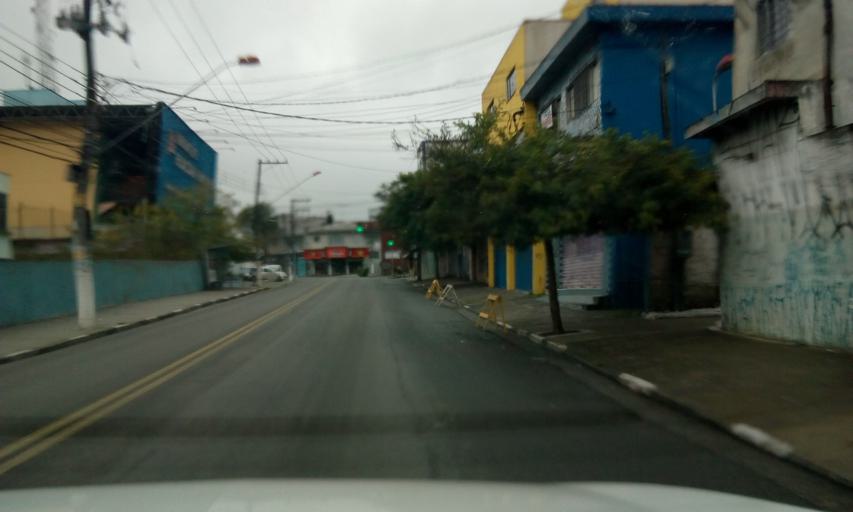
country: BR
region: Sao Paulo
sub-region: Diadema
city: Diadema
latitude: -23.6931
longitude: -46.6243
